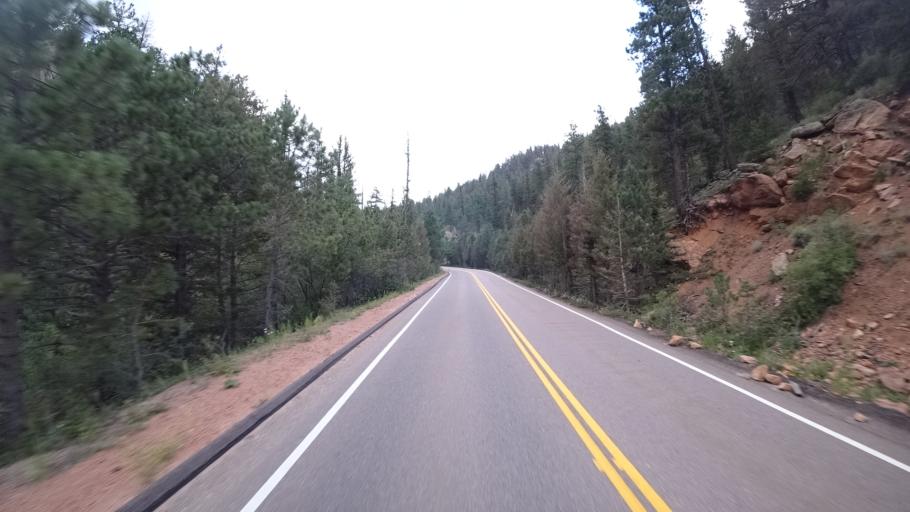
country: US
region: Colorado
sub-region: El Paso County
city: Cascade-Chipita Park
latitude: 38.8988
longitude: -104.9874
